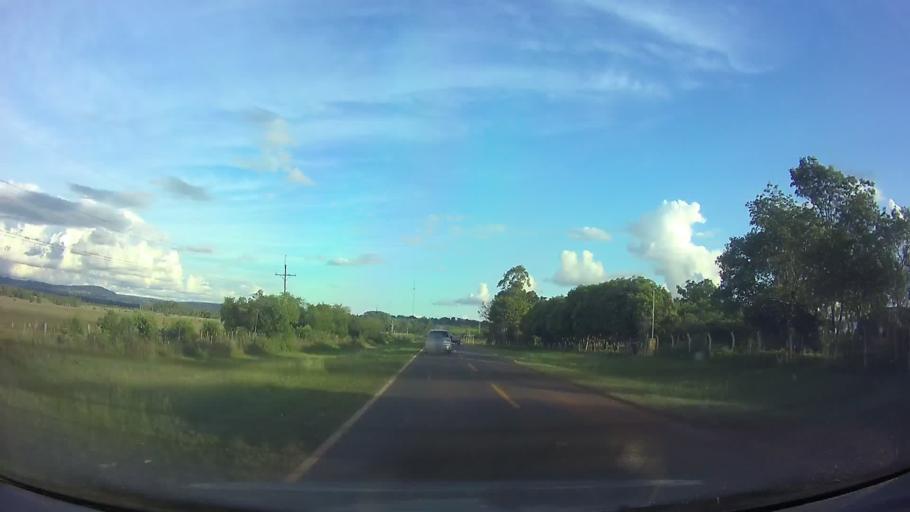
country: PY
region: Paraguari
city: Ybycui
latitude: -26.0009
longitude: -57.0458
